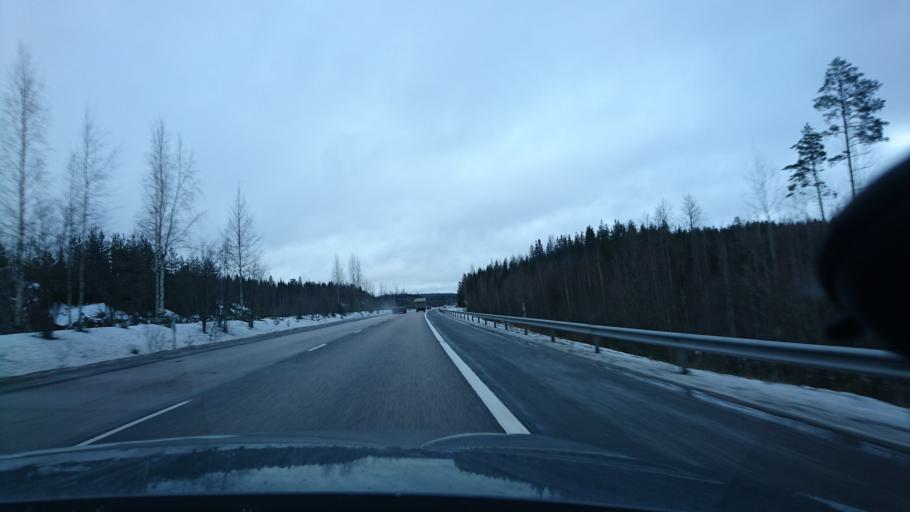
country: FI
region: Uusimaa
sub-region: Porvoo
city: Pukkila
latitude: 60.7561
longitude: 25.4605
